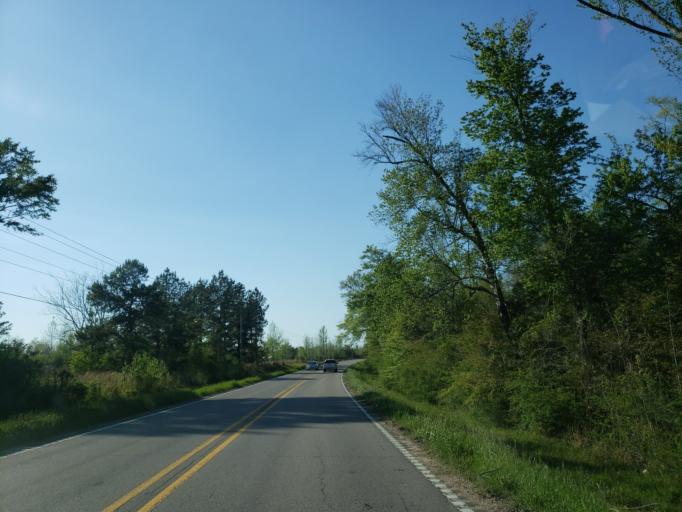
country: US
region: Mississippi
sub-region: Perry County
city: Richton
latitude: 31.4634
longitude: -88.9891
